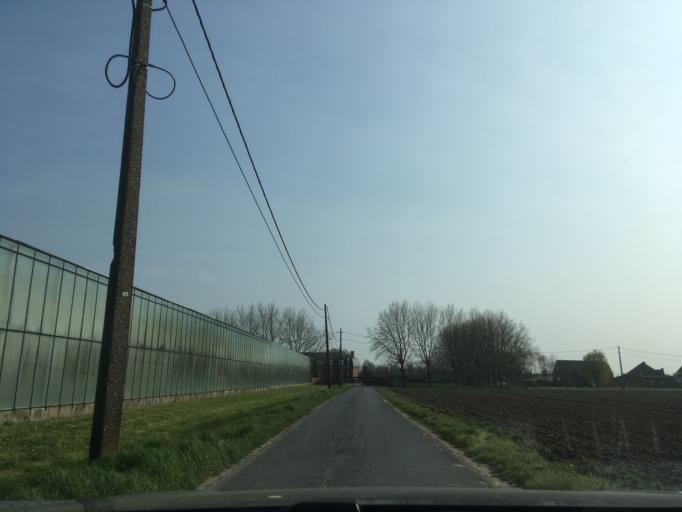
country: BE
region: Flanders
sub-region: Provincie West-Vlaanderen
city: Ardooie
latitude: 50.9929
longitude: 3.2117
